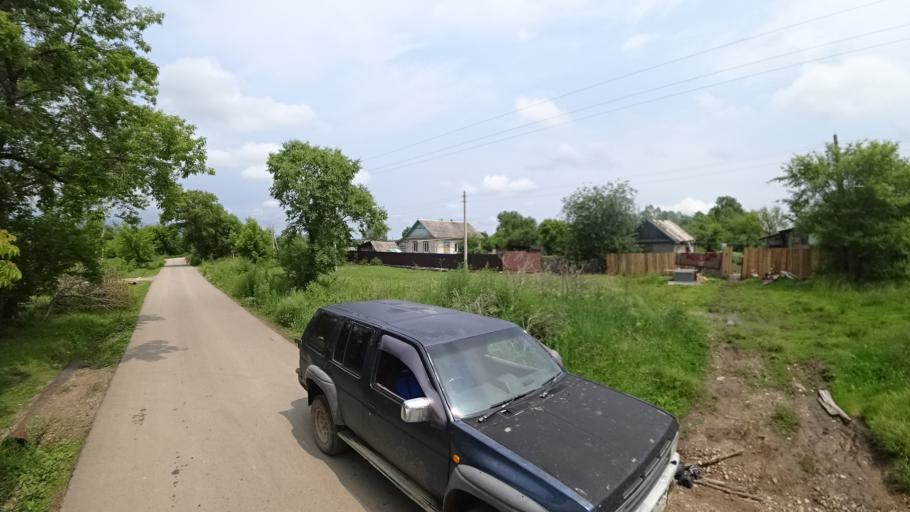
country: RU
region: Primorskiy
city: Novosysoyevka
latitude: 44.2379
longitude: 133.3583
